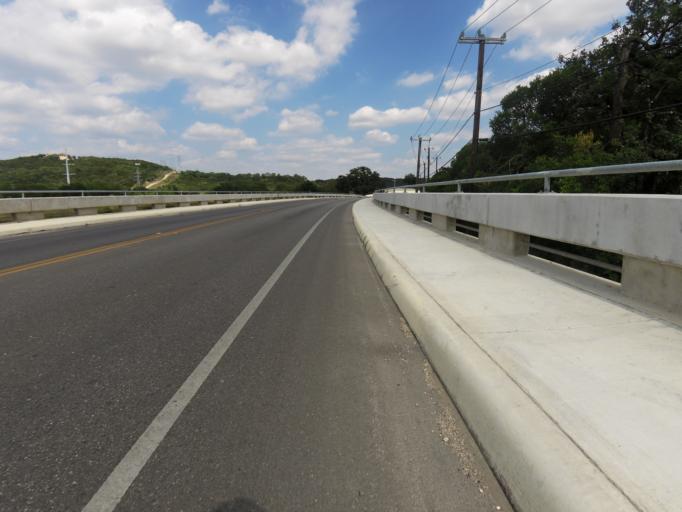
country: US
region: Texas
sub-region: Bexar County
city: Cross Mountain
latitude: 29.6128
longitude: -98.6319
